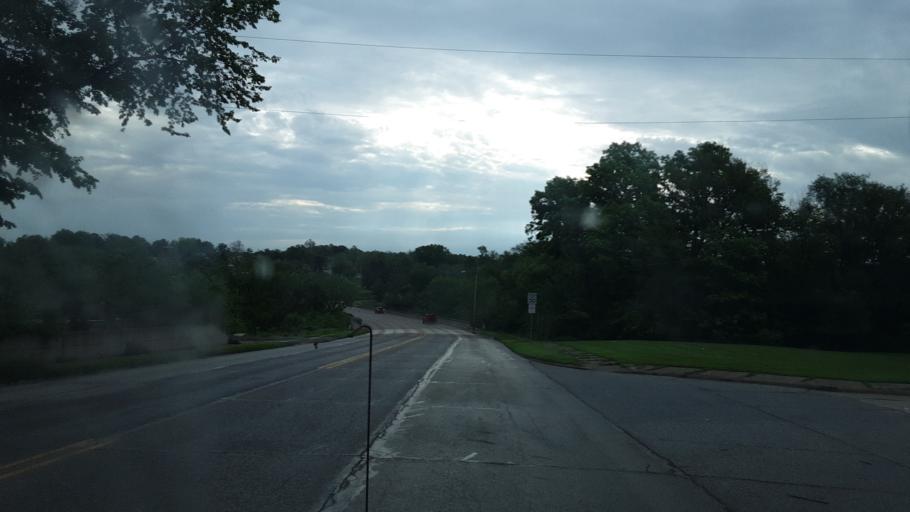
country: US
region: Iowa
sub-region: Lee County
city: Keokuk
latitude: 40.3914
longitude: -91.3965
